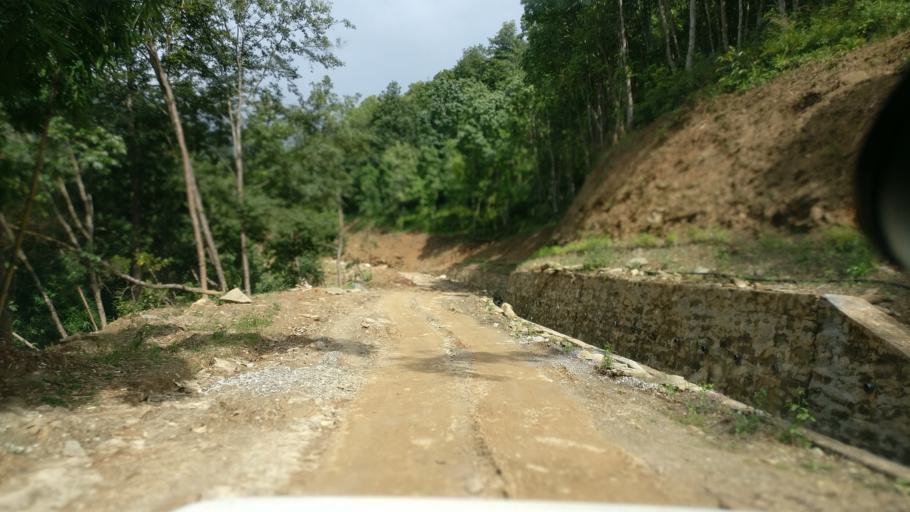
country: NP
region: Western Region
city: Baglung
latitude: 28.2663
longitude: 83.6460
